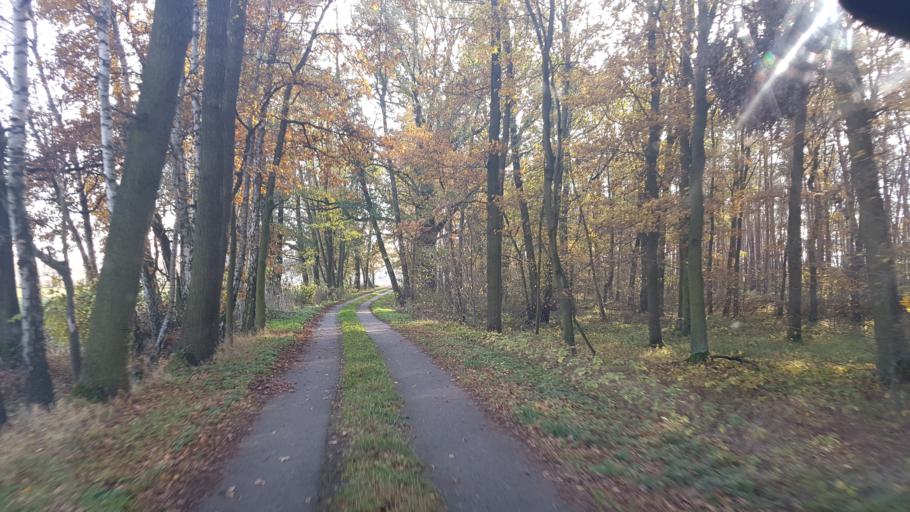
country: DE
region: Brandenburg
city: Falkenberg
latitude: 51.6212
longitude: 13.2967
